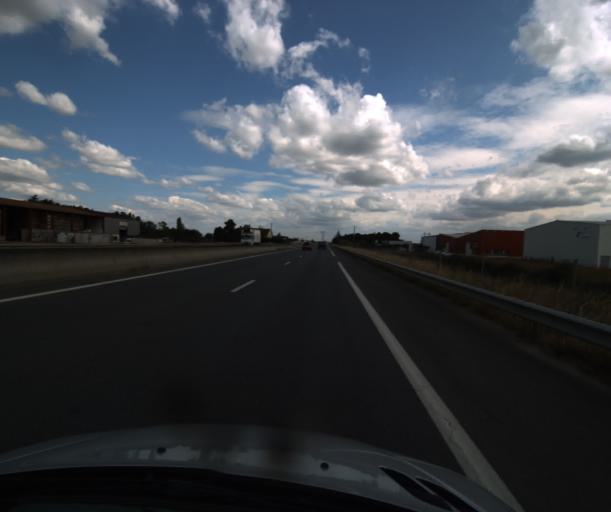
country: FR
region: Midi-Pyrenees
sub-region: Departement du Tarn-et-Garonne
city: Bressols
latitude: 43.9472
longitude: 1.3241
